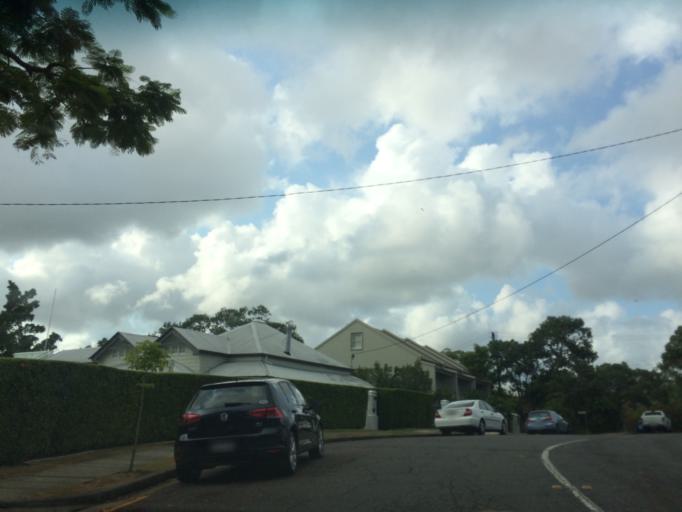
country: AU
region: Queensland
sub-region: Brisbane
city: Toowong
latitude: -27.4953
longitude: 152.9975
